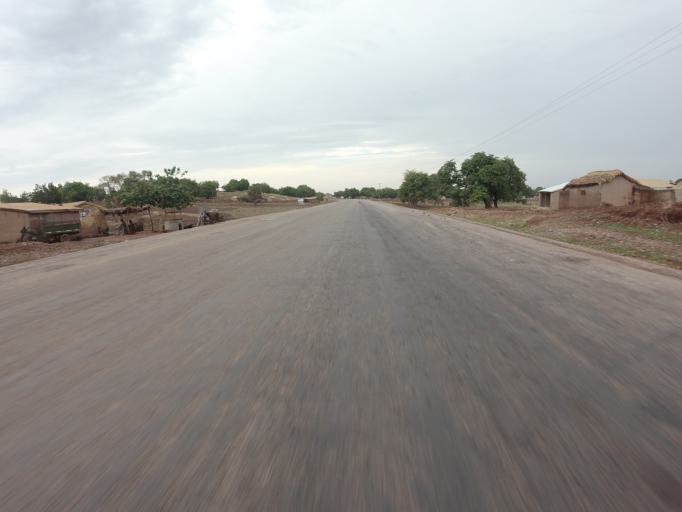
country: GH
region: Upper East
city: Bolgatanga
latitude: 10.8544
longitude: -0.6712
